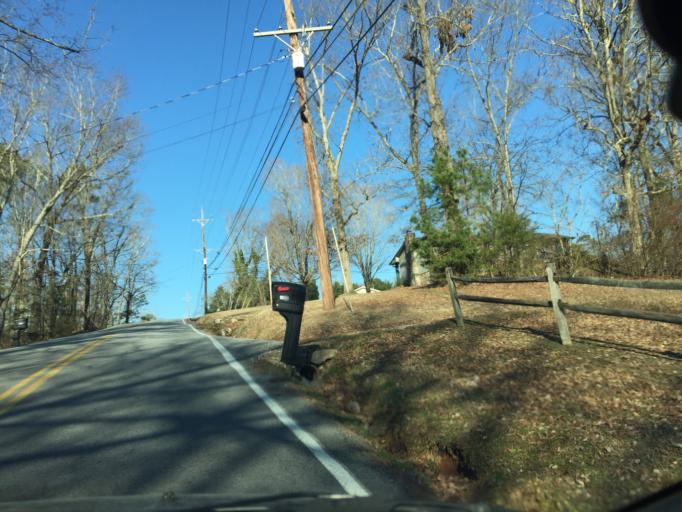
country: US
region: Tennessee
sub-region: Hamilton County
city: Collegedale
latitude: 35.0354
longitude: -85.0828
